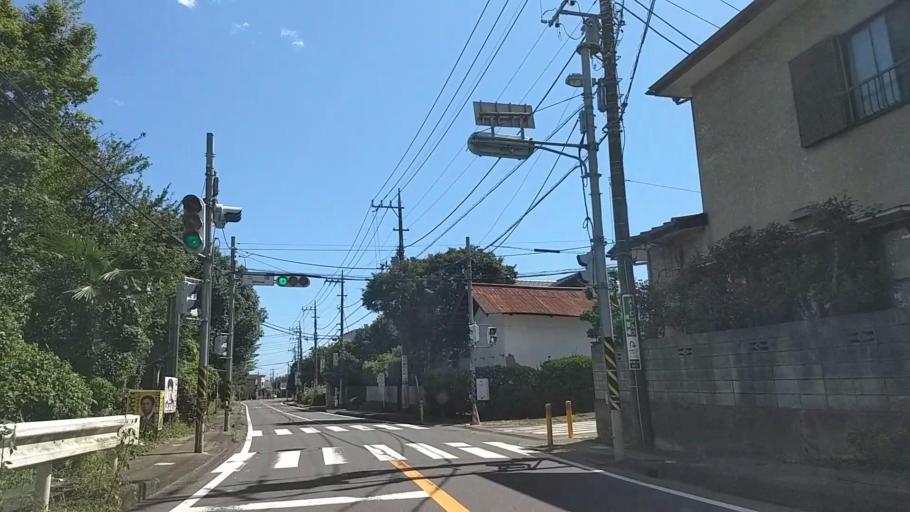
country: JP
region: Kanagawa
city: Zama
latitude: 35.5400
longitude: 139.3044
